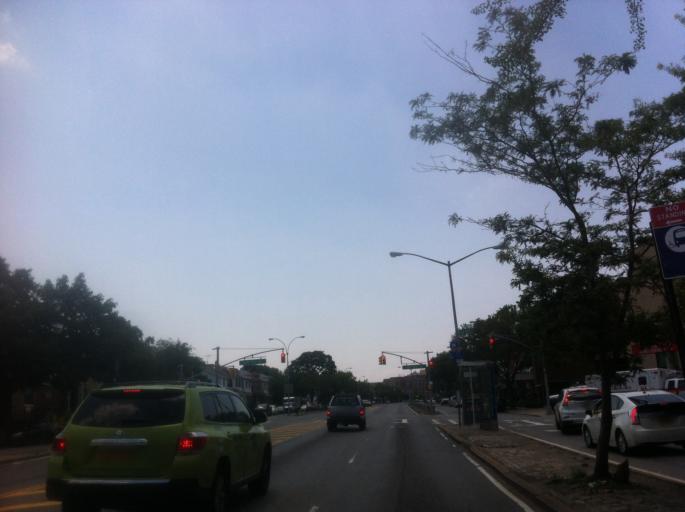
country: US
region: New York
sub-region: Kings County
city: Brooklyn
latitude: 40.6206
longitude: -73.9409
